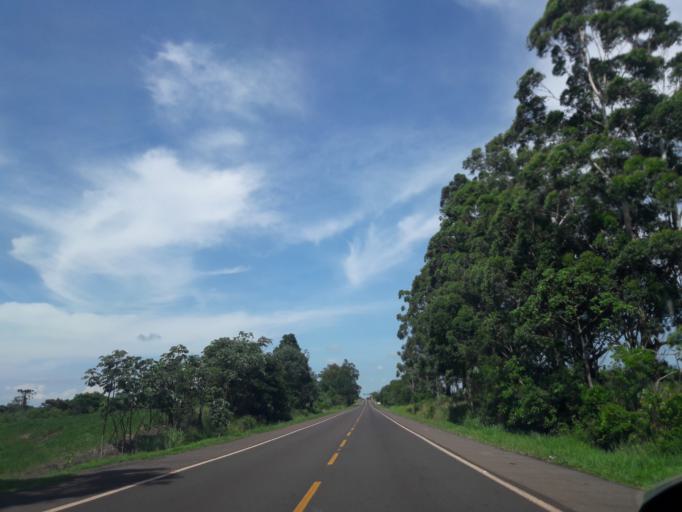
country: BR
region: Parana
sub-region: Campo Mourao
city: Campo Mourao
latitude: -24.2788
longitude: -52.5293
